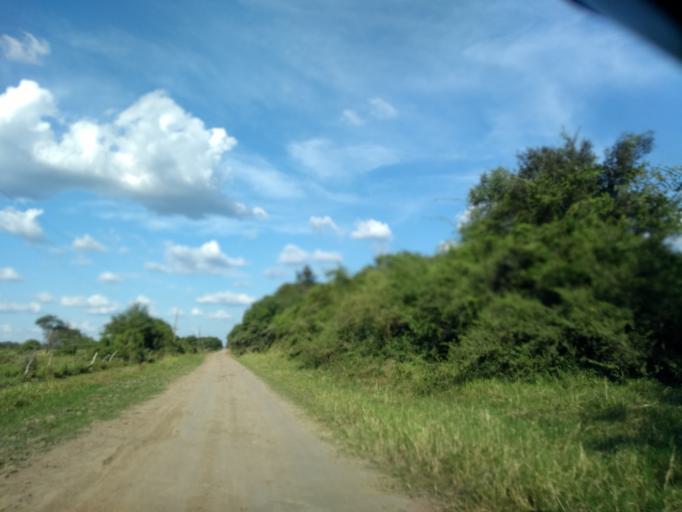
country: AR
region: Chaco
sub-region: Departamento de Quitilipi
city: Quitilipi
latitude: -26.7581
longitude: -60.2400
